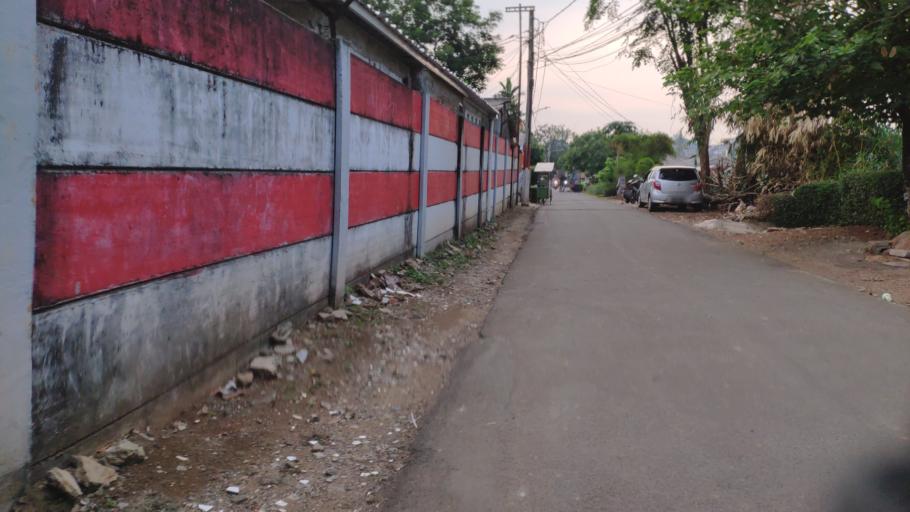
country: ID
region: West Java
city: Pamulang
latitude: -6.2980
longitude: 106.8074
